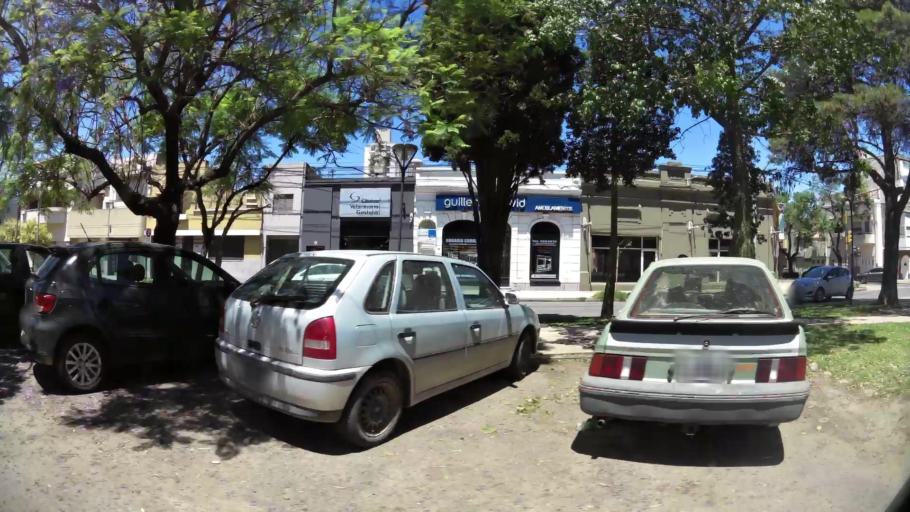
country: AR
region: Santa Fe
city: Santa Fe de la Vera Cruz
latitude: -31.6337
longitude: -60.7121
